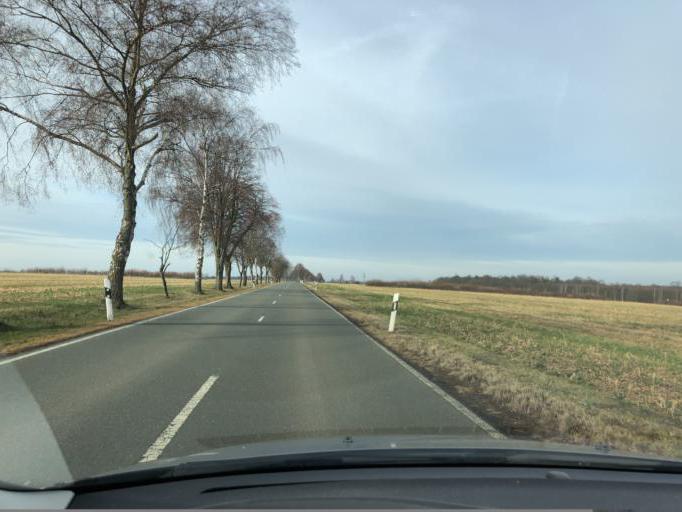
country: DE
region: Saxony-Anhalt
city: Bad Bibra
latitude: 51.1850
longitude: 11.5330
